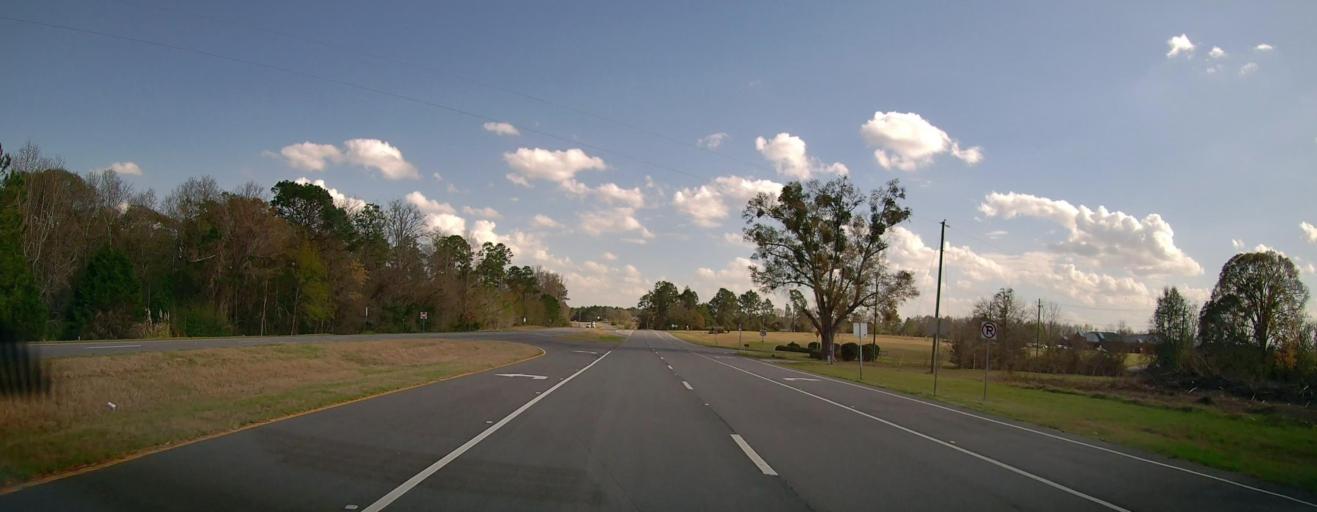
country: US
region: Georgia
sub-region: Telfair County
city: McRae
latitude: 32.0518
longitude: -82.8617
